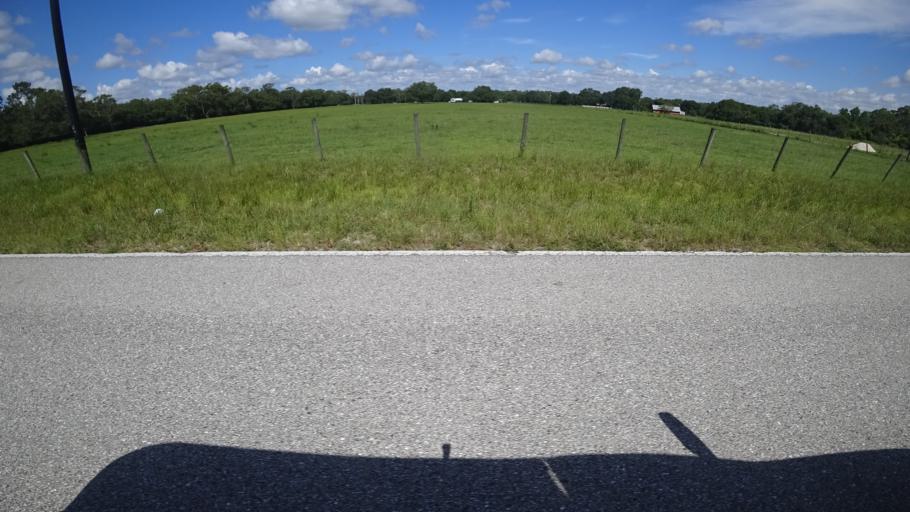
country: US
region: Florida
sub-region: Sarasota County
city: Lake Sarasota
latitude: 27.3366
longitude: -82.1627
